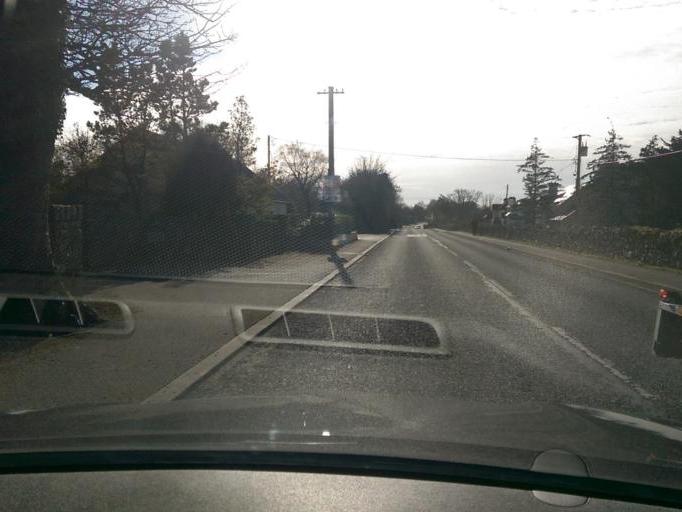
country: IE
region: Connaught
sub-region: County Galway
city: Oranmore
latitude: 53.2510
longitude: -8.9413
